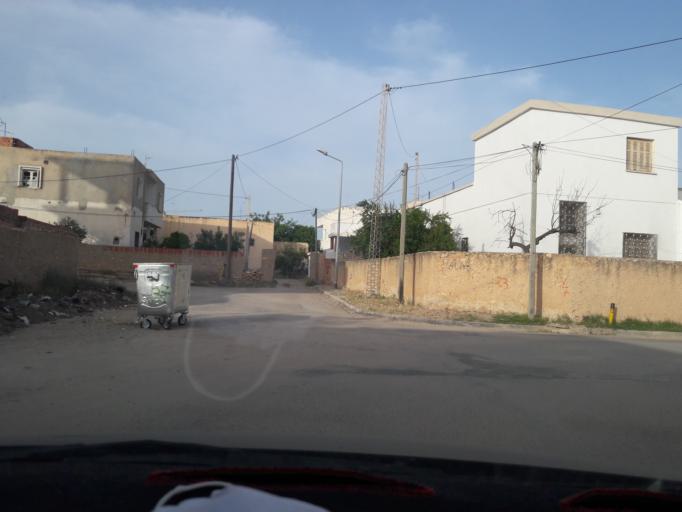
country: TN
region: Safaqis
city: Al Qarmadah
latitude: 34.8026
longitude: 10.7554
